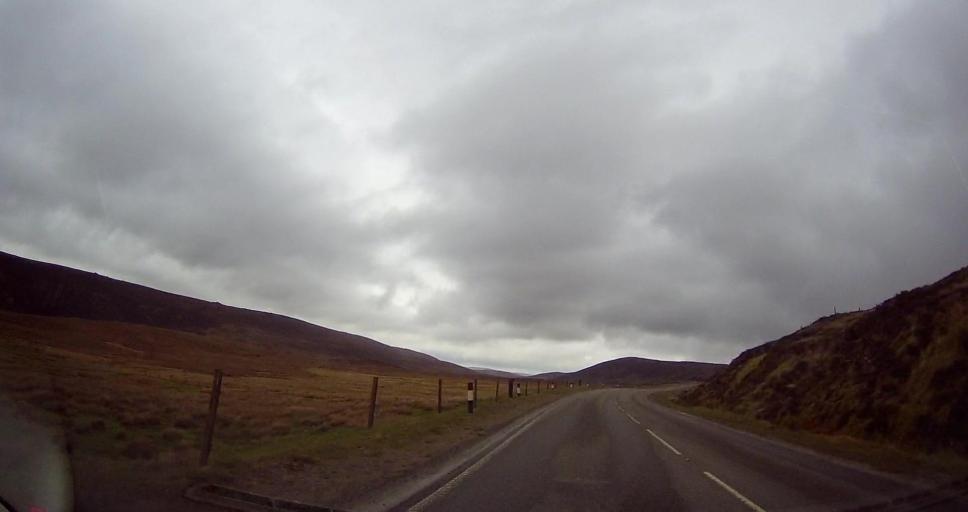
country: GB
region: Scotland
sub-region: Shetland Islands
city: Lerwick
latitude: 60.2876
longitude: -1.2414
